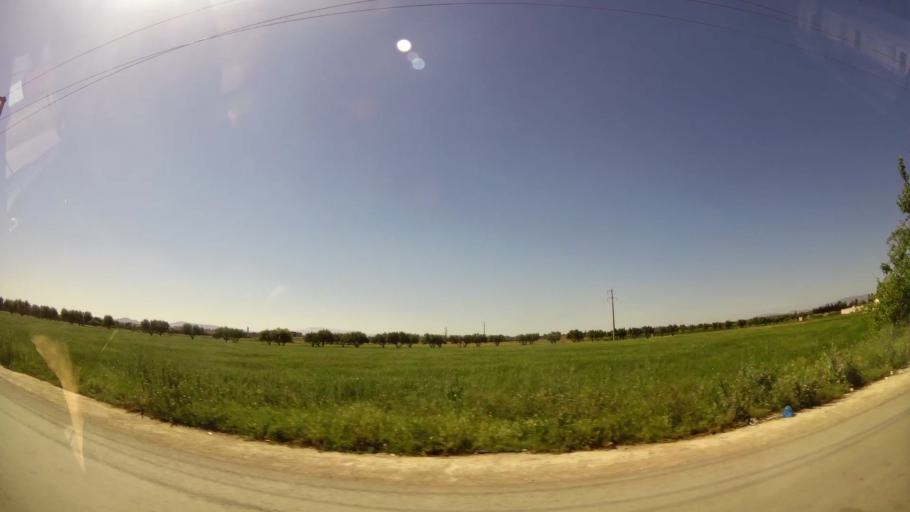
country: MA
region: Oriental
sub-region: Oujda-Angad
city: Oujda
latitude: 34.7078
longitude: -1.8650
